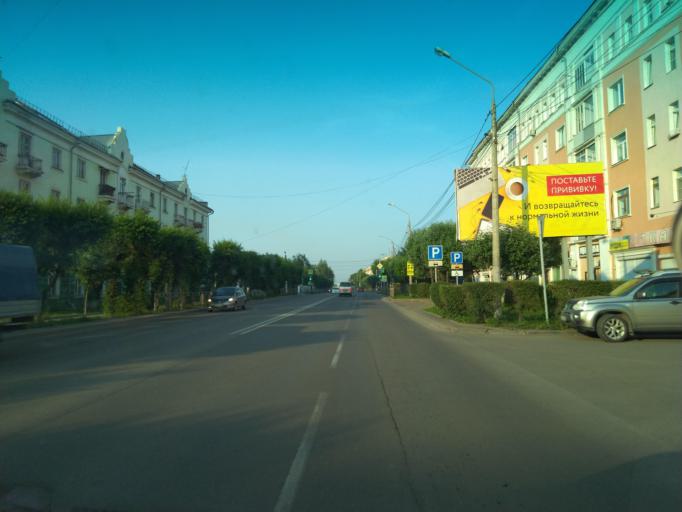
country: RU
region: Krasnoyarskiy
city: Krasnoyarsk
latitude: 55.9989
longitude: 92.9348
